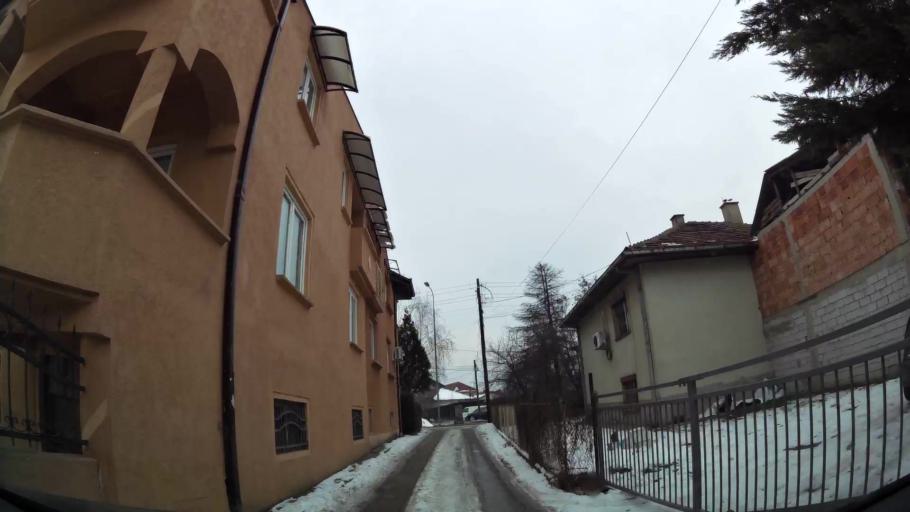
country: MK
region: Butel
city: Butel
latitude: 42.0399
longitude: 21.4488
